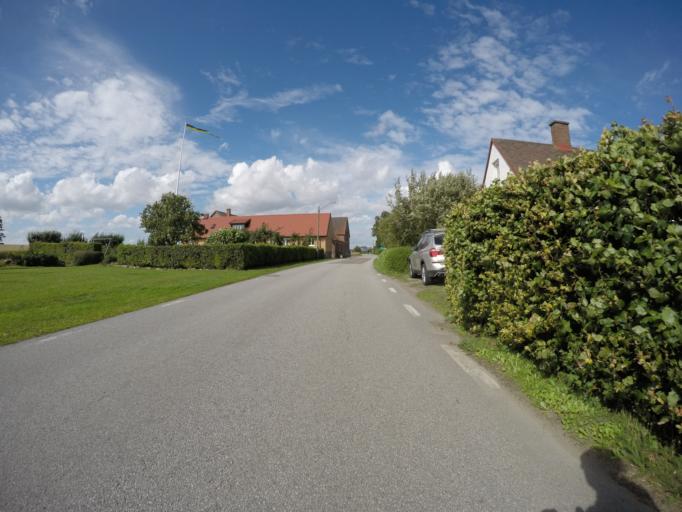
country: SE
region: Skane
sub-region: Simrishamns Kommun
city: Simrishamn
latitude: 55.4983
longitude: 14.2032
